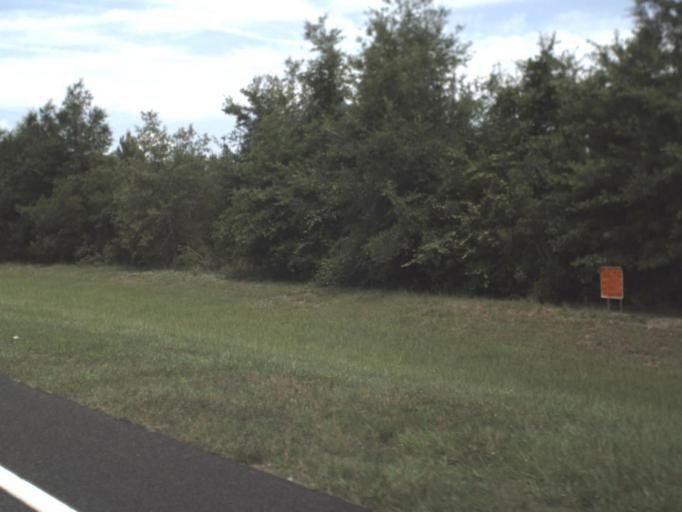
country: US
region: Florida
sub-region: Alachua County
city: Hawthorne
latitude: 29.6019
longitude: -82.2016
